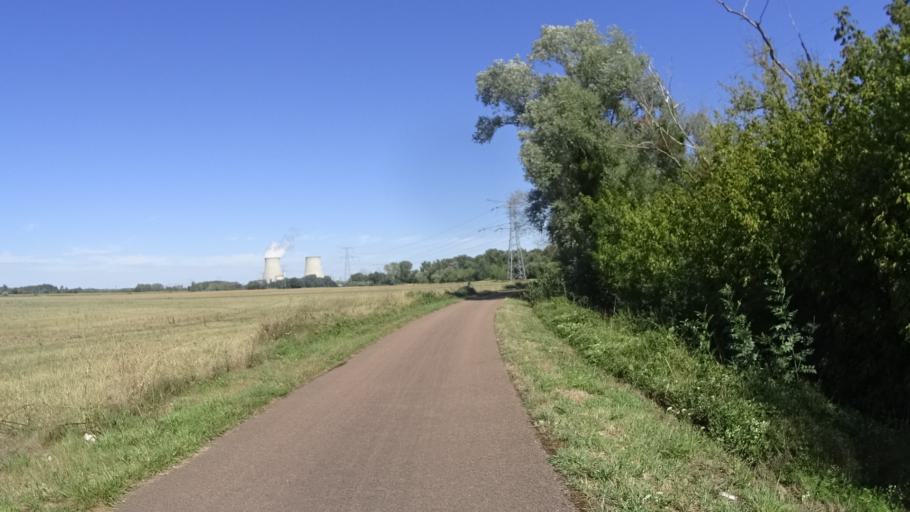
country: FR
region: Centre
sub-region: Departement du Cher
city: Lere
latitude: 47.4885
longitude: 2.8927
